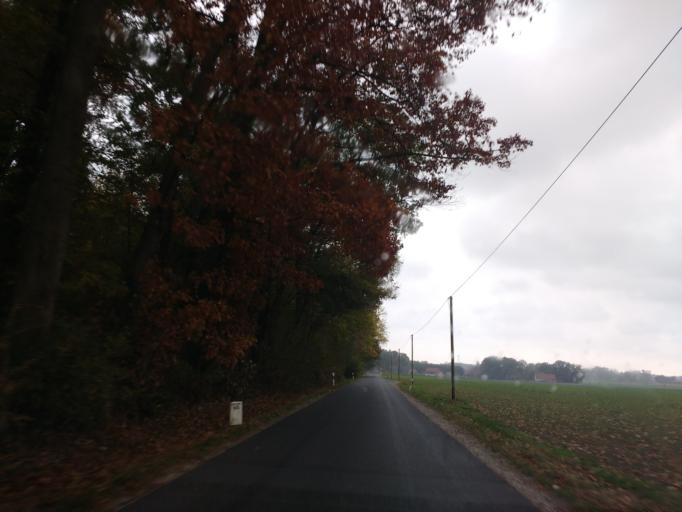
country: DE
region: North Rhine-Westphalia
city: Borgholzhausen
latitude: 52.0749
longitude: 8.2963
